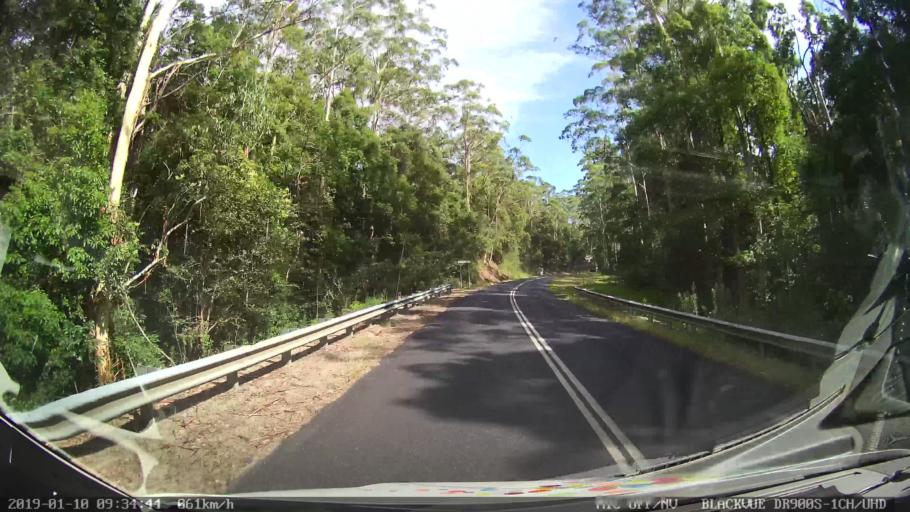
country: AU
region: New South Wales
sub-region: Coffs Harbour
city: Nana Glen
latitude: -30.2172
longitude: 153.0097
